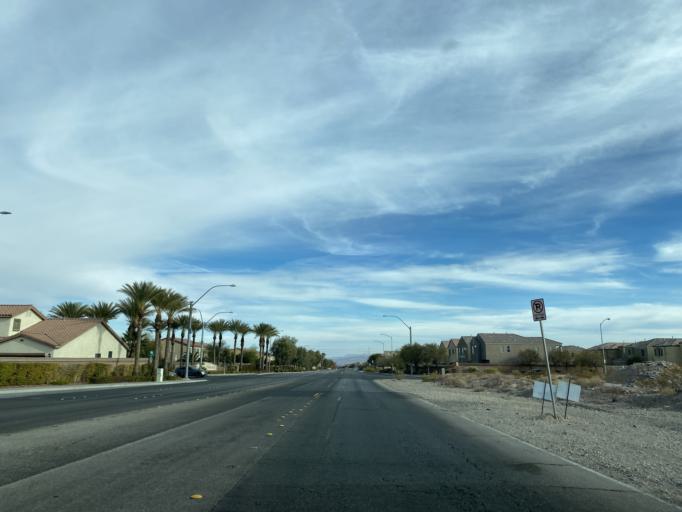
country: US
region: Nevada
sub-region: Clark County
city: Enterprise
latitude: 36.0411
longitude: -115.2533
